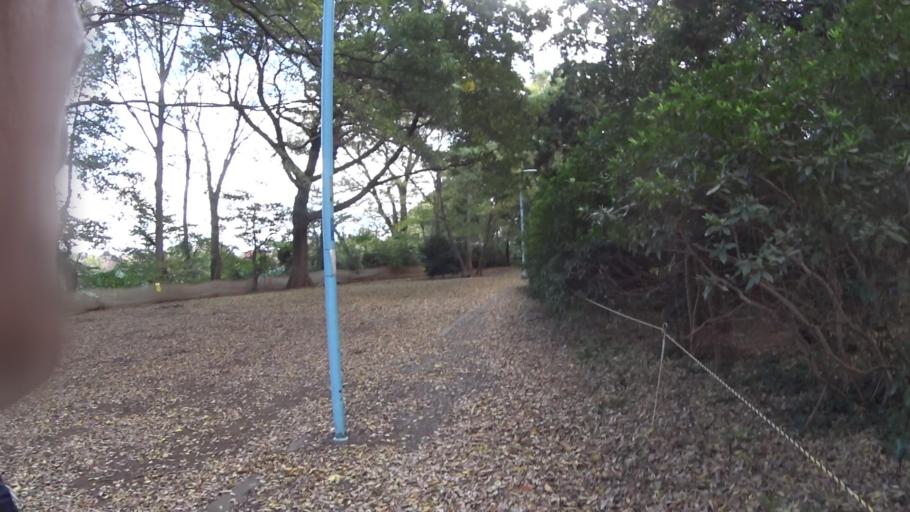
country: JP
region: Tokyo
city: Tokyo
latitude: 35.6829
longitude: 139.6418
